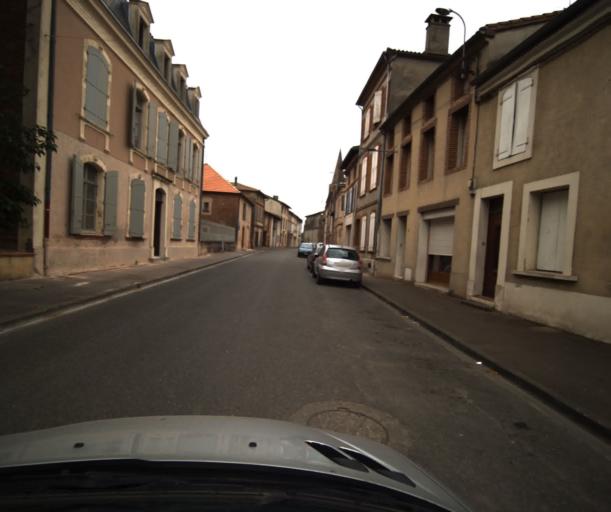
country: FR
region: Midi-Pyrenees
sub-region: Departement du Tarn-et-Garonne
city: Saint-Nicolas-de-la-Grave
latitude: 44.0651
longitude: 1.0211
